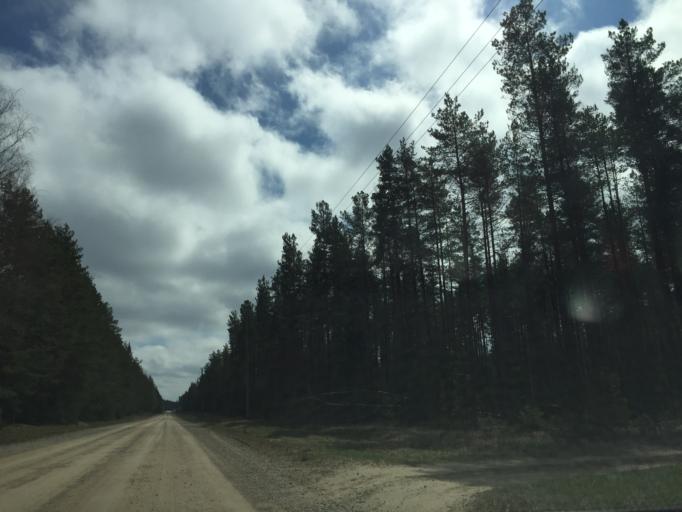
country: EE
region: Valgamaa
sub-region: Valga linn
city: Valga
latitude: 57.6589
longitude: 26.2053
